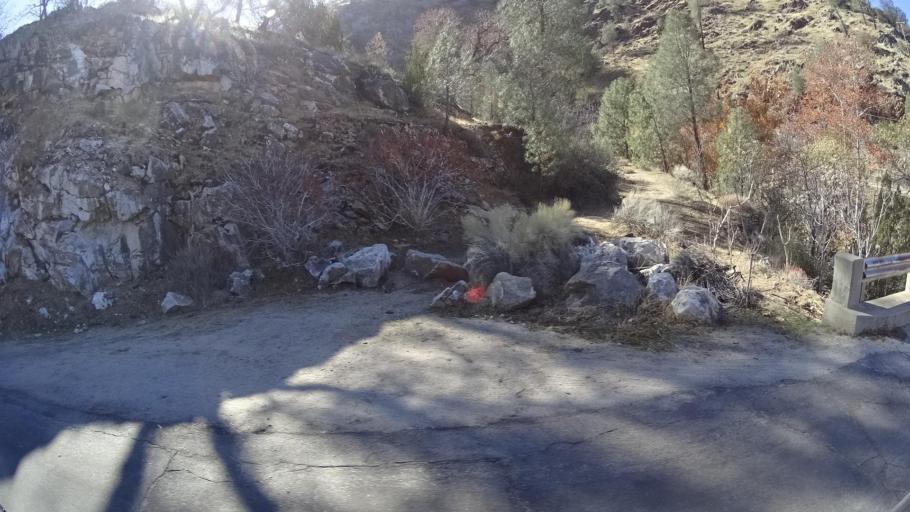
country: US
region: California
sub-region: Kern County
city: Bodfish
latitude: 35.5741
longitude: -118.5299
